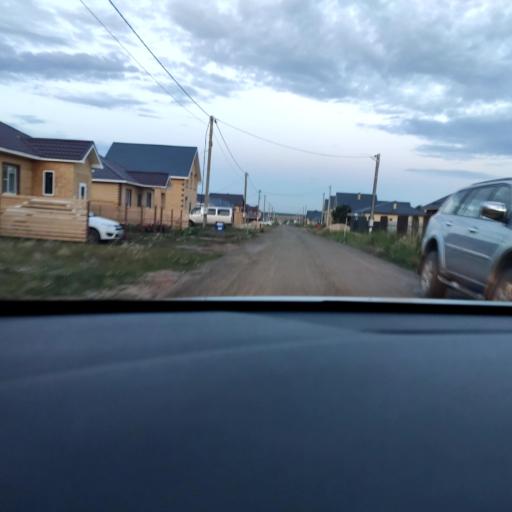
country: RU
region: Tatarstan
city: Stolbishchi
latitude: 55.7168
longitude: 49.2986
